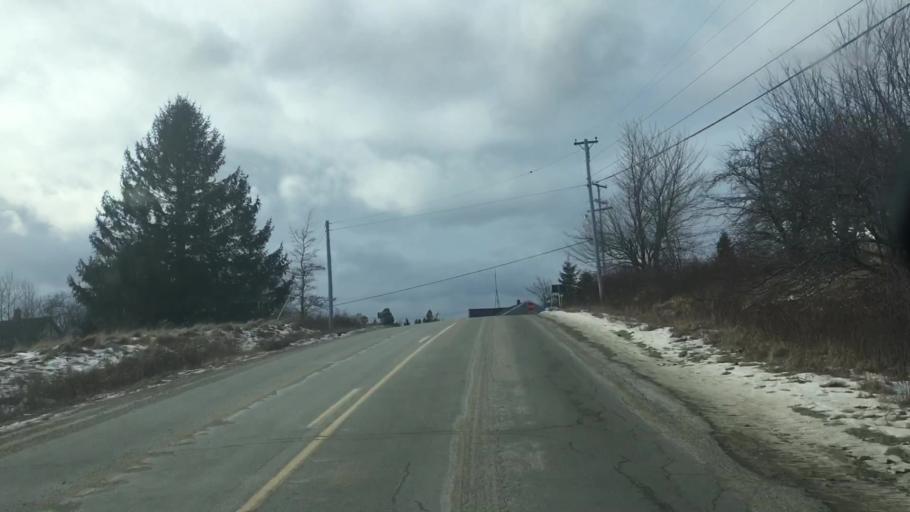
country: US
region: Maine
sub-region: Washington County
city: Machias
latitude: 44.6633
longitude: -67.5540
